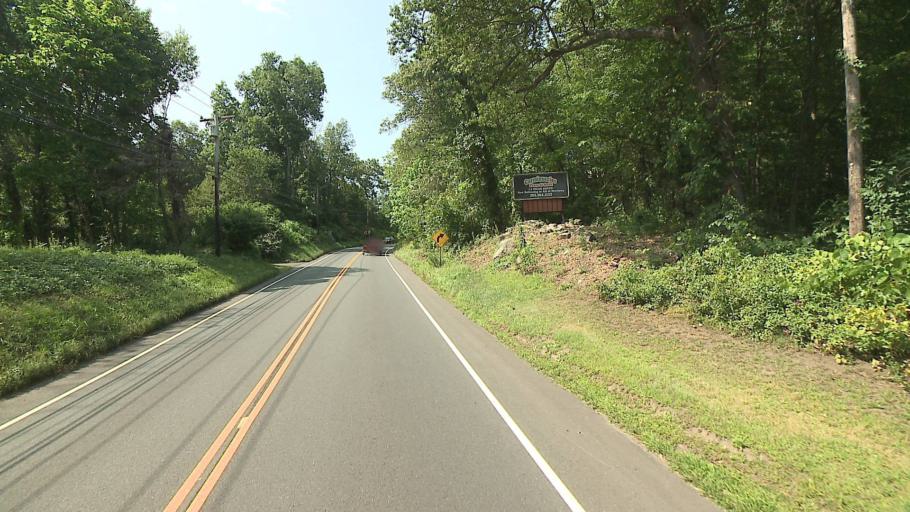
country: US
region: Connecticut
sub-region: Fairfield County
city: Newtown
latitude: 41.3564
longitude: -73.2629
